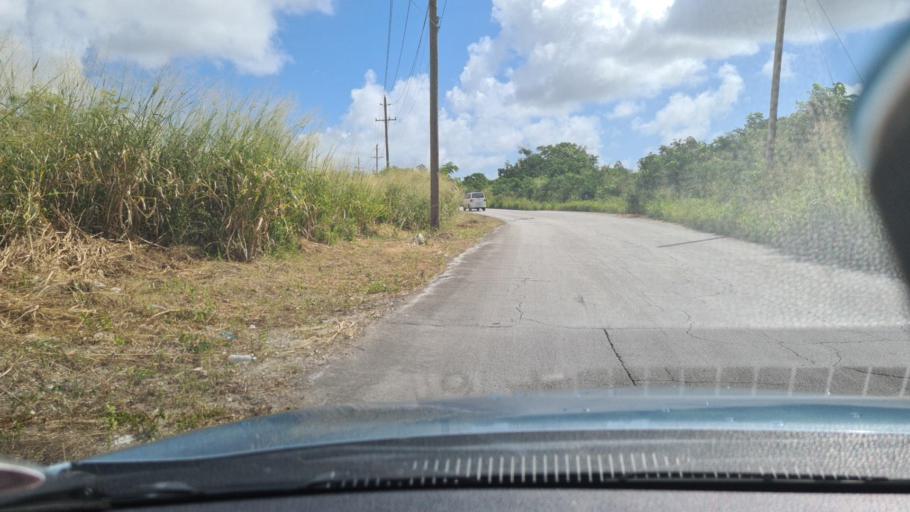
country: BB
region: Christ Church
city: Oistins
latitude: 13.0829
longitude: -59.5548
